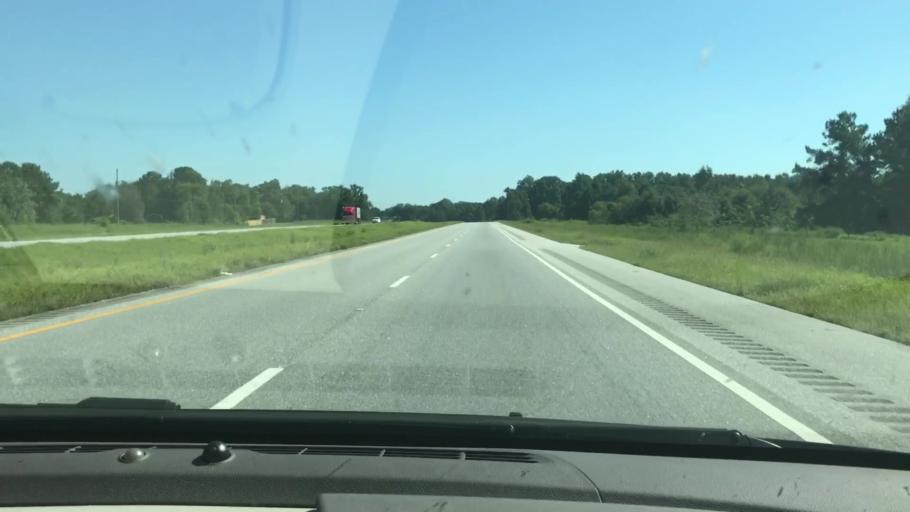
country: US
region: Alabama
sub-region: Russell County
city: Ladonia
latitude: 32.3631
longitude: -85.1013
